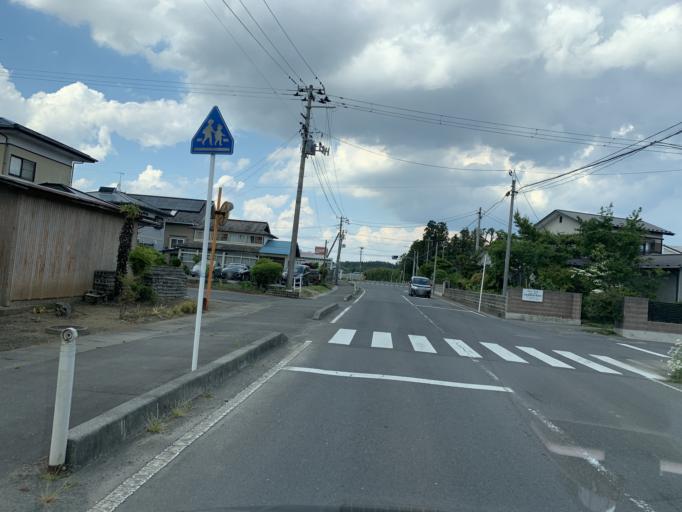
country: JP
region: Miyagi
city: Wakuya
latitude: 38.6298
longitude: 141.2006
